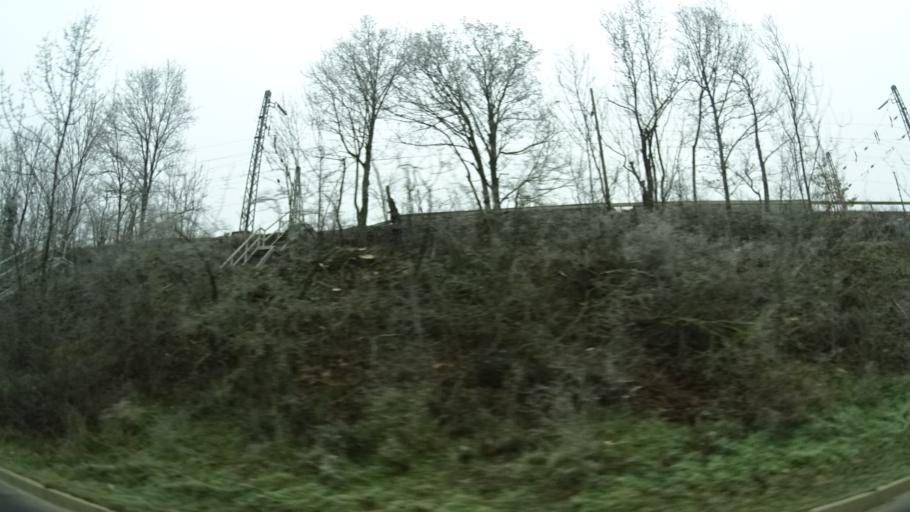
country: DE
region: Bavaria
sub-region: Regierungsbezirk Unterfranken
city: Kitzingen
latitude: 49.7280
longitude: 10.1577
